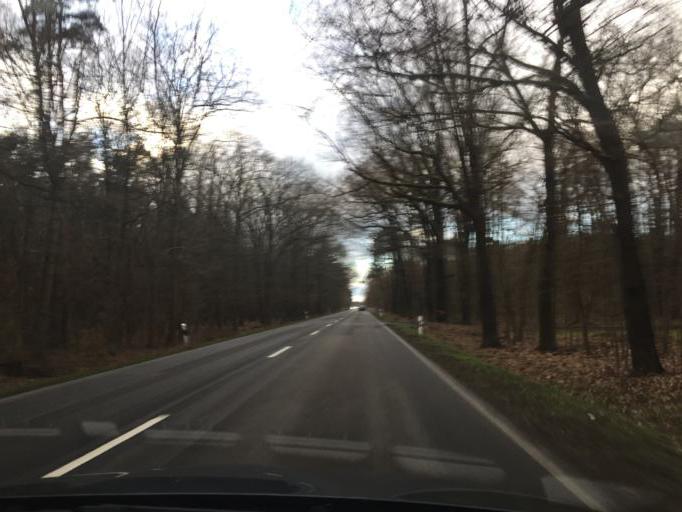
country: DE
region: Brandenburg
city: Werben
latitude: 51.7556
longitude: 14.1784
